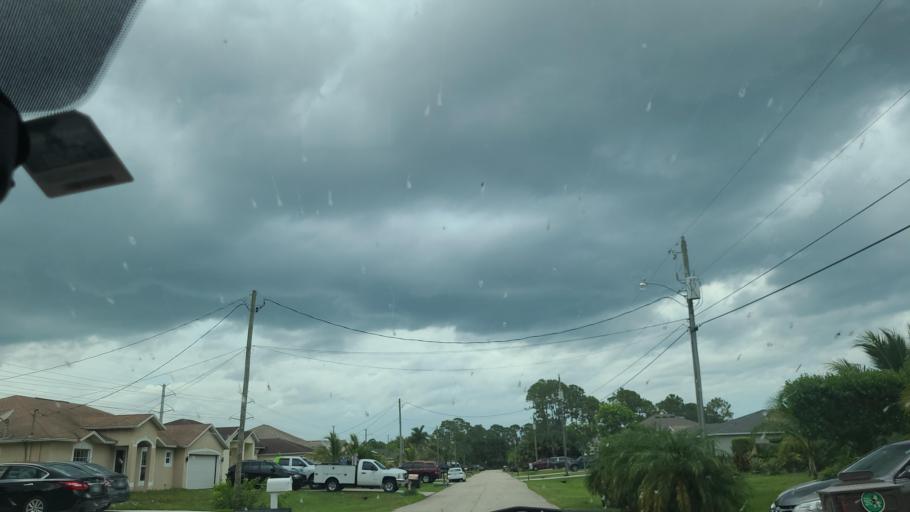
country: US
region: Florida
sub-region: Saint Lucie County
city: Port Saint Lucie
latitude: 27.2504
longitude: -80.4148
